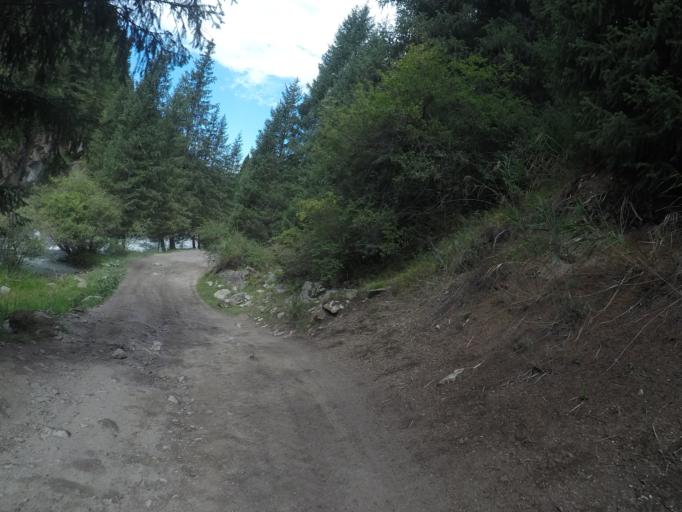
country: KG
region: Ysyk-Koel
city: Teploklyuchenka
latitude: 42.4422
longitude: 78.5544
